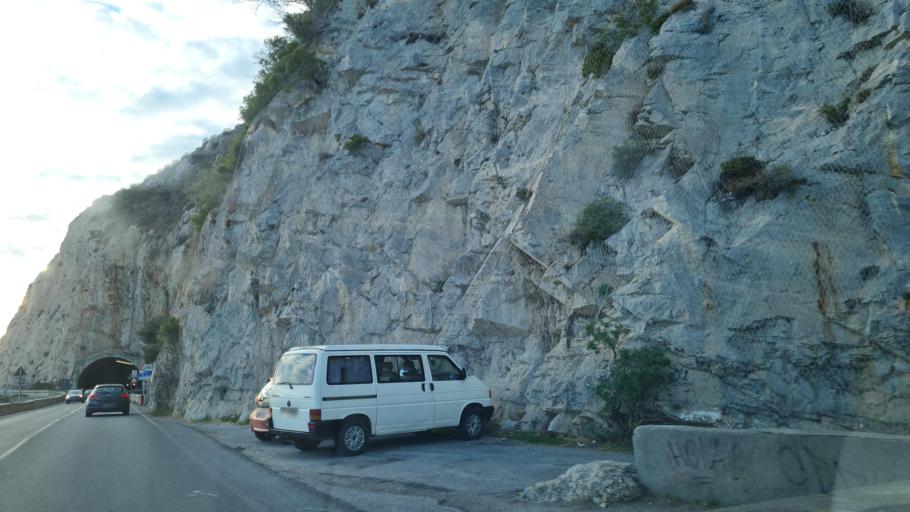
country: IT
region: Liguria
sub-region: Provincia di Savona
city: Noli
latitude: 44.1910
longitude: 8.4162
